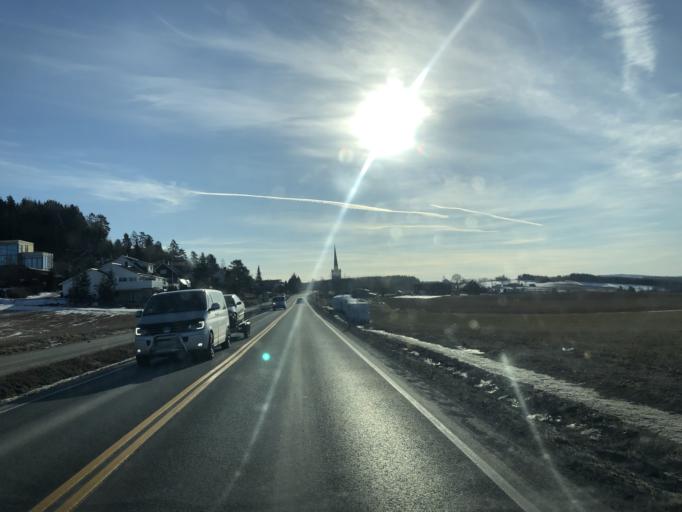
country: NO
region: Hedmark
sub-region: Ringsaker
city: Moelv
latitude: 60.9064
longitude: 10.7158
